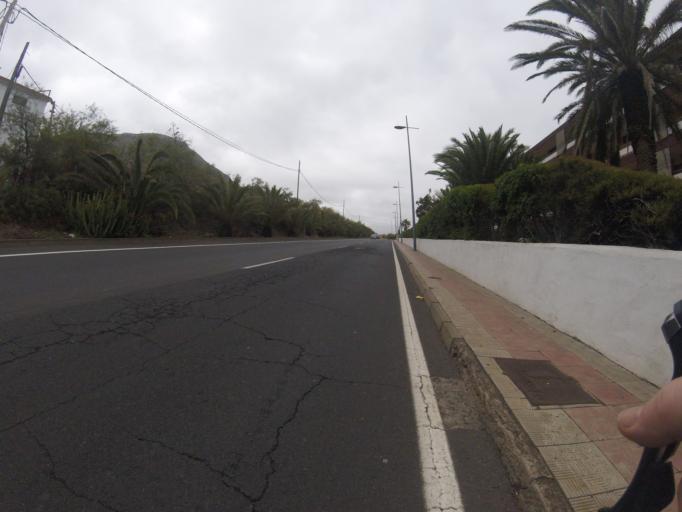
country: ES
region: Canary Islands
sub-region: Provincia de Santa Cruz de Tenerife
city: Tegueste
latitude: 28.5517
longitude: -16.3478
